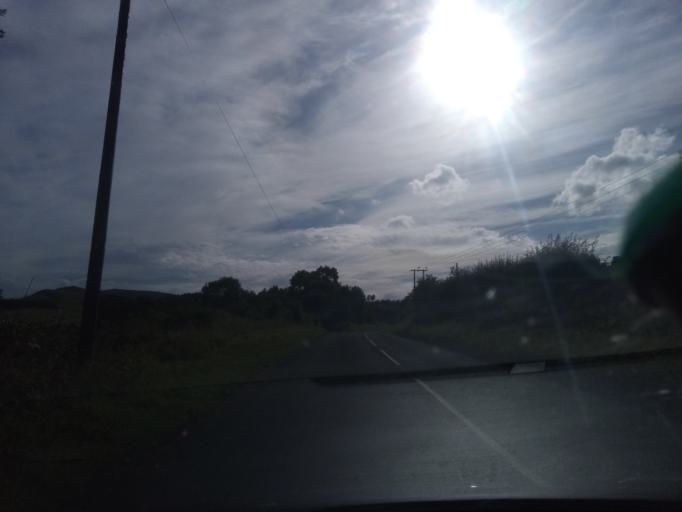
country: GB
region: Scotland
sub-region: The Scottish Borders
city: Coldstream
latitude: 55.5331
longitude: -2.2958
